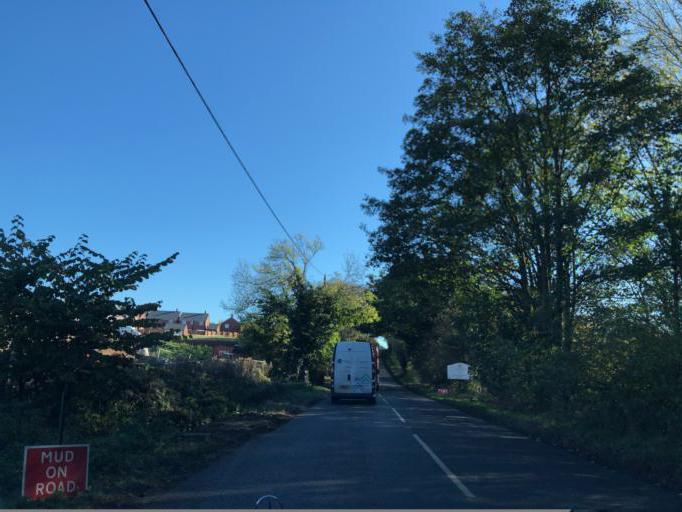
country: GB
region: England
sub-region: Warwickshire
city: Royal Leamington Spa
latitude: 52.2600
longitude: -1.5333
